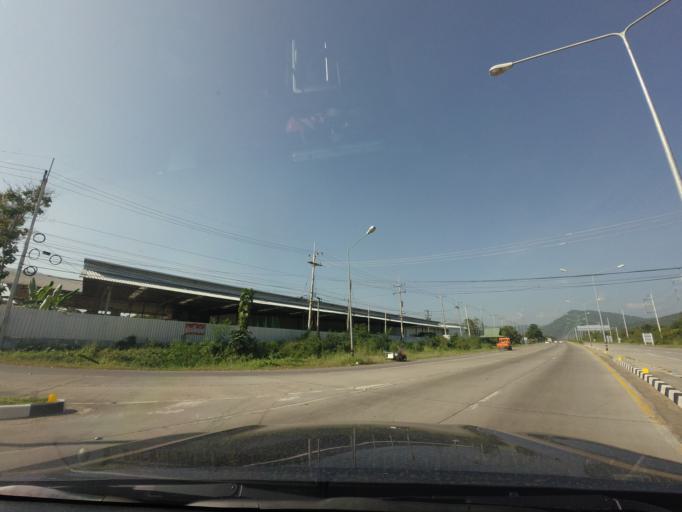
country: TH
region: Phetchabun
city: Lom Sak
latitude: 16.7689
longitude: 101.1713
